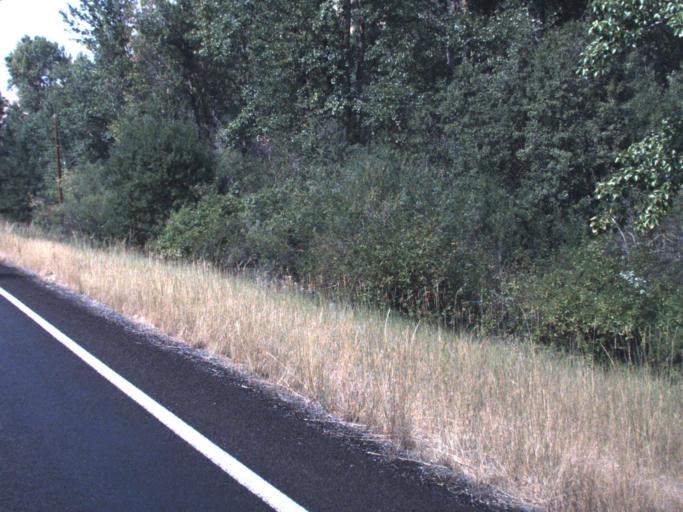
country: US
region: Washington
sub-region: Kittitas County
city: Ellensburg
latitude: 47.0668
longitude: -120.6531
